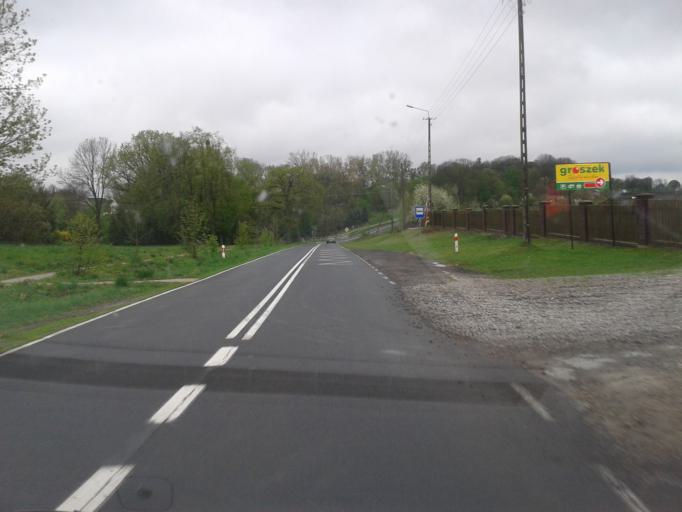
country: PL
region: Lublin Voivodeship
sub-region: Powiat hrubieszowski
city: Mircze
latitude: 50.5582
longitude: 23.9370
